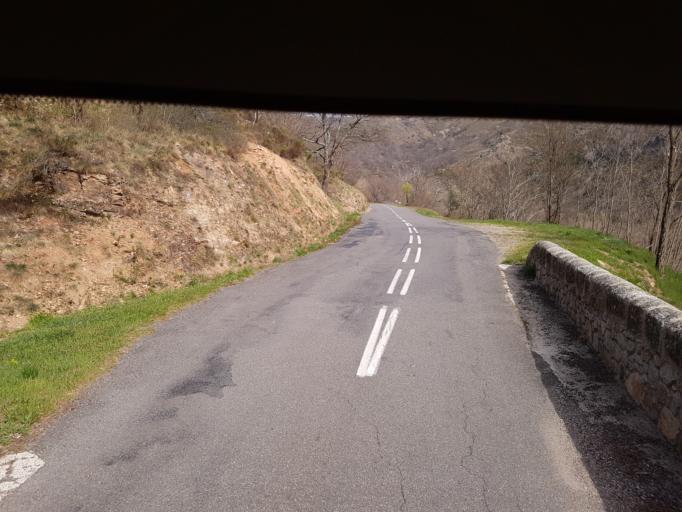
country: FR
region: Languedoc-Roussillon
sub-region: Departement de la Lozere
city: Florac
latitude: 44.3573
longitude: 3.6613
